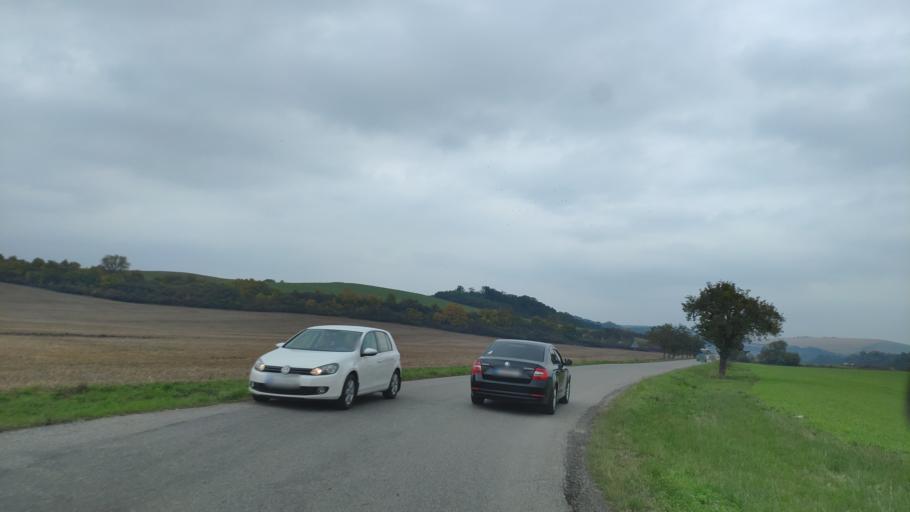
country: SK
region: Kosicky
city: Kosice
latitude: 48.6393
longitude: 21.3730
